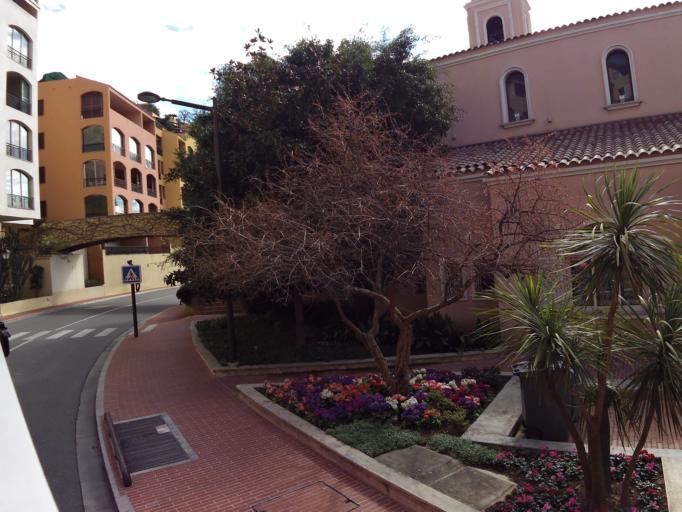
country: MC
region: Commune de Monaco
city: Fontvieille
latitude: 43.7282
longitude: 7.4182
